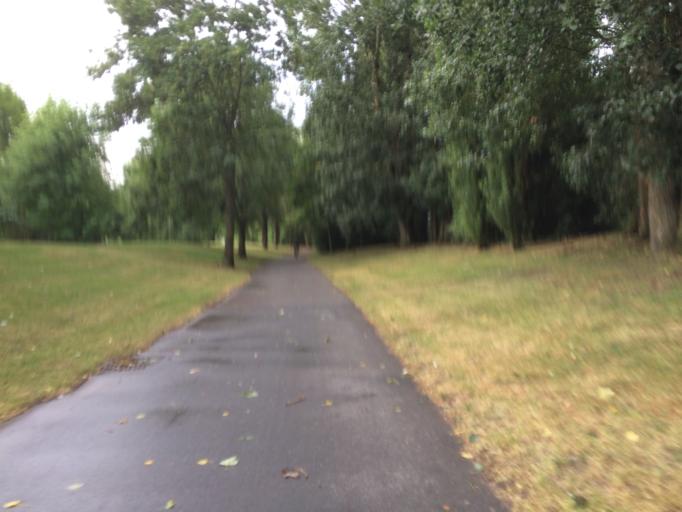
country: FR
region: Picardie
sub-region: Departement de l'Oise
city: Venette
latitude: 49.4071
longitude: 2.7981
